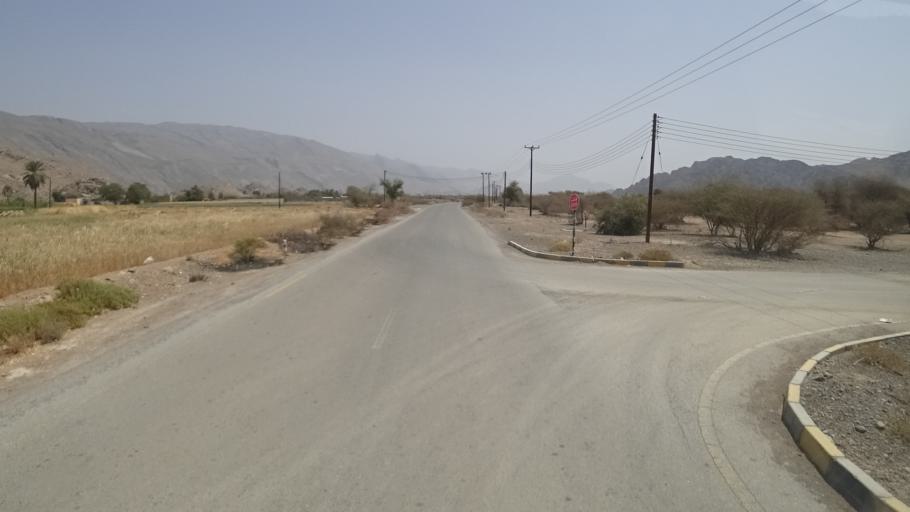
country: OM
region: Muhafazat ad Dakhiliyah
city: Nizwa
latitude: 23.0421
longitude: 57.4471
